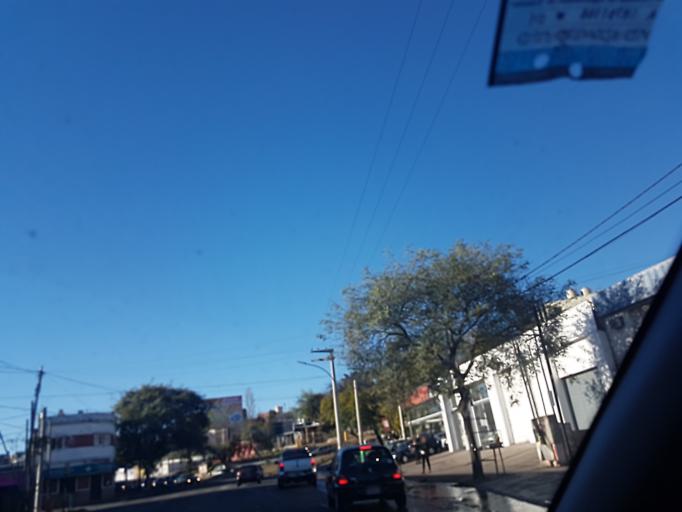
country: AR
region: Cordoba
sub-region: Departamento de Capital
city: Cordoba
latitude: -31.3901
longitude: -64.2033
